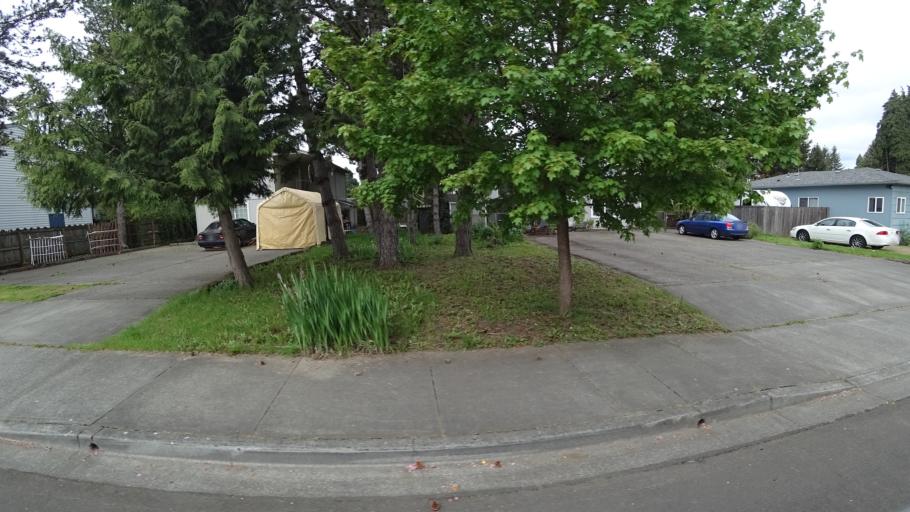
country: US
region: Oregon
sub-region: Washington County
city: Hillsboro
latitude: 45.5258
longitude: -122.9928
